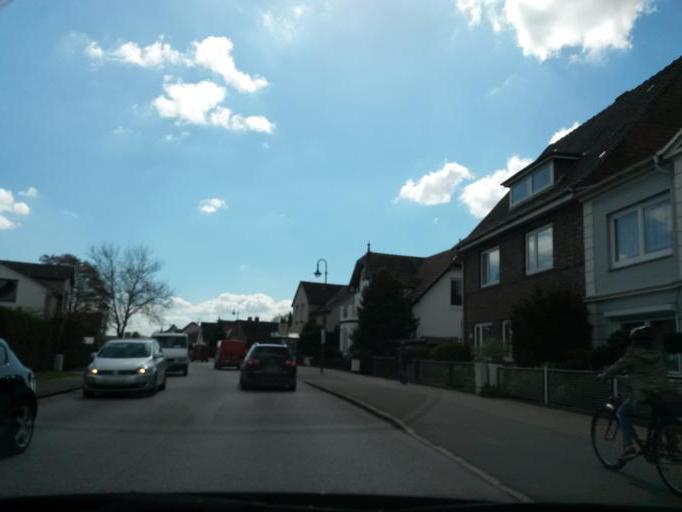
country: DE
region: Schleswig-Holstein
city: Moorrege
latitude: 53.6756
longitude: 9.6763
